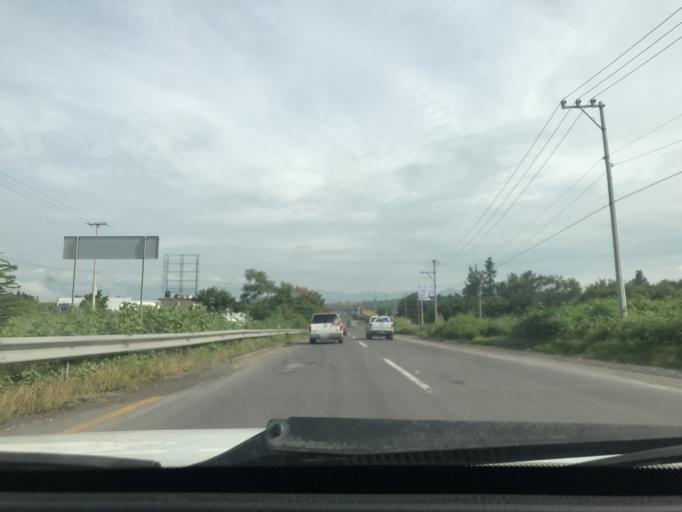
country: MX
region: Morelos
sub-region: Yecapixtla
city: Juan Morales
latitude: 18.8272
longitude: -98.9219
